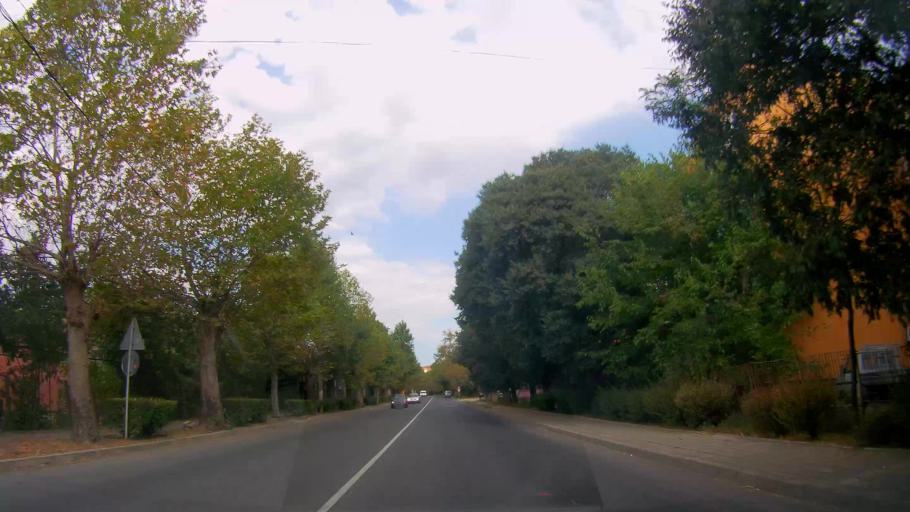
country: BG
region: Burgas
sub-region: Obshtina Aytos
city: Aytos
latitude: 42.7000
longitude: 27.2481
